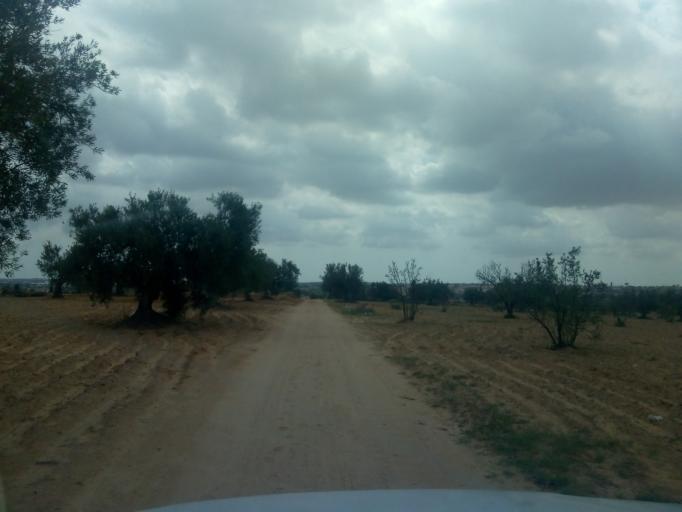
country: TN
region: Safaqis
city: Sfax
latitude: 34.7466
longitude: 10.4891
